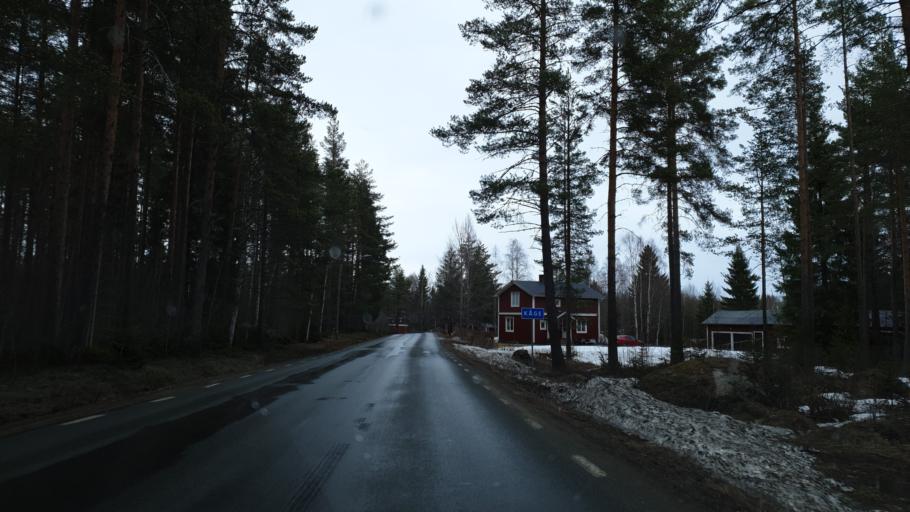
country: SE
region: Vaesterbotten
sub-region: Skelleftea Kommun
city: Kage
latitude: 64.8259
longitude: 20.9841
